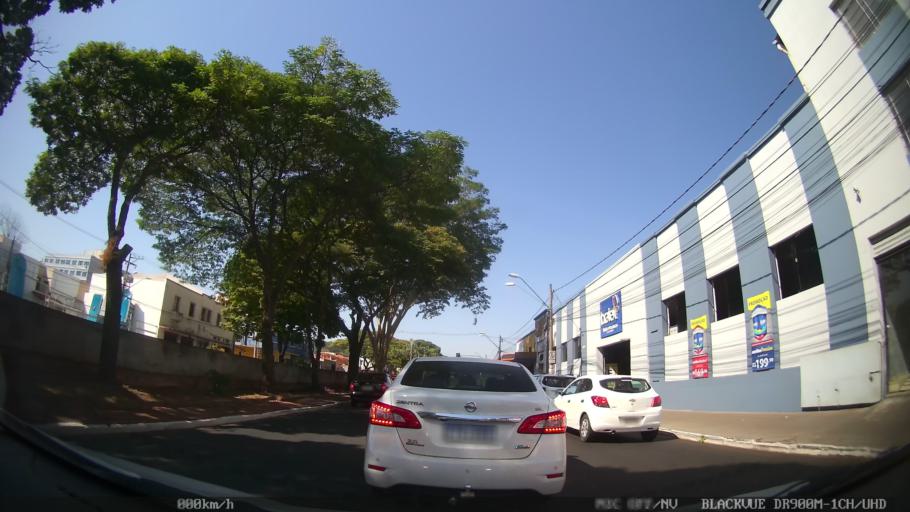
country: BR
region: Sao Paulo
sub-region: Ribeirao Preto
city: Ribeirao Preto
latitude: -21.1700
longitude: -47.8101
